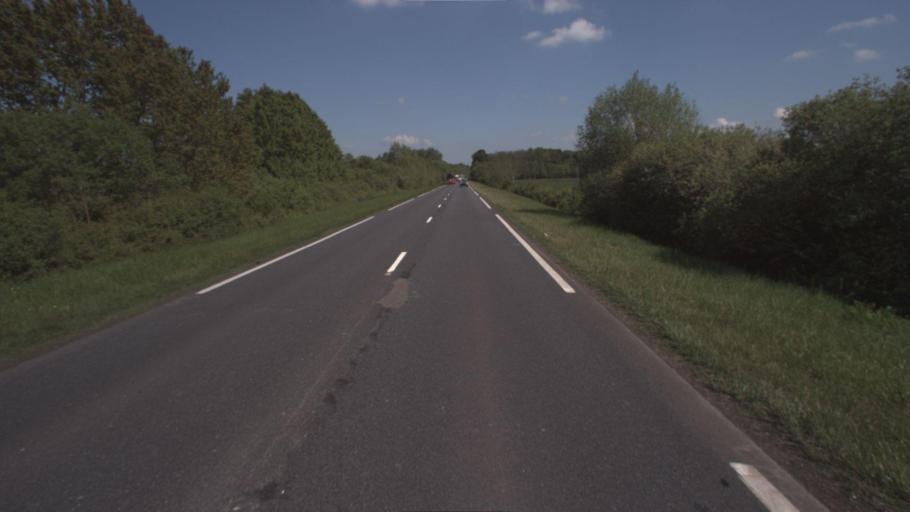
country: FR
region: Ile-de-France
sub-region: Departement de Seine-et-Marne
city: Chaumes-en-Brie
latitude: 48.6786
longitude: 2.8140
